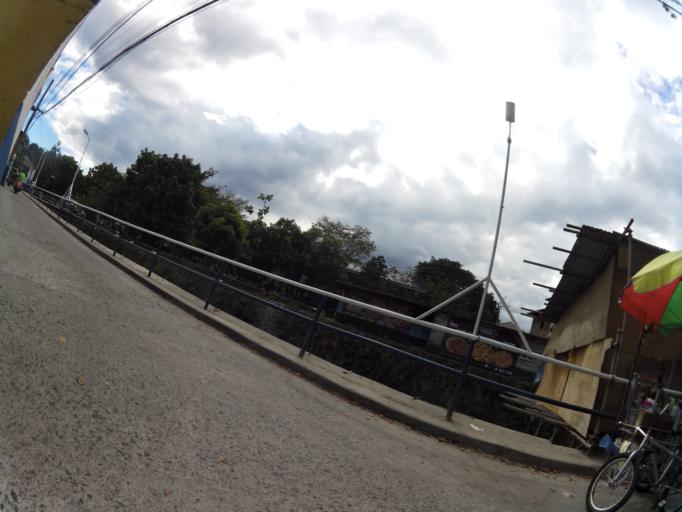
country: PH
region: Metro Manila
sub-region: Marikina
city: Calumpang
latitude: 14.6266
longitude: 121.1040
